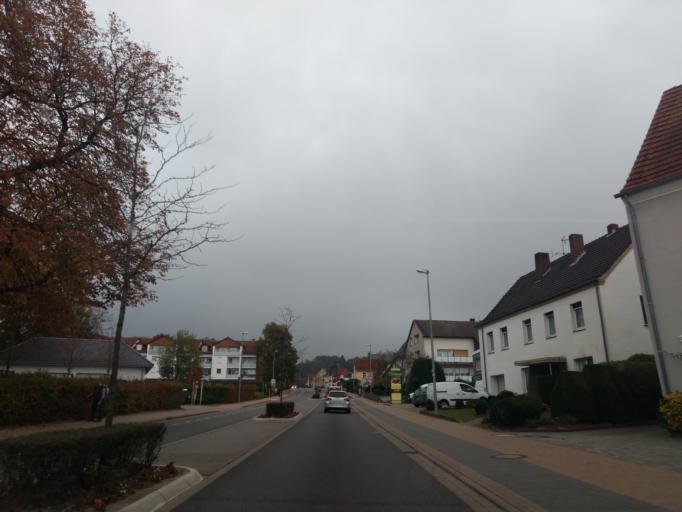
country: DE
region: Lower Saxony
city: Bad Iburg
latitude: 52.1606
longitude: 8.0487
